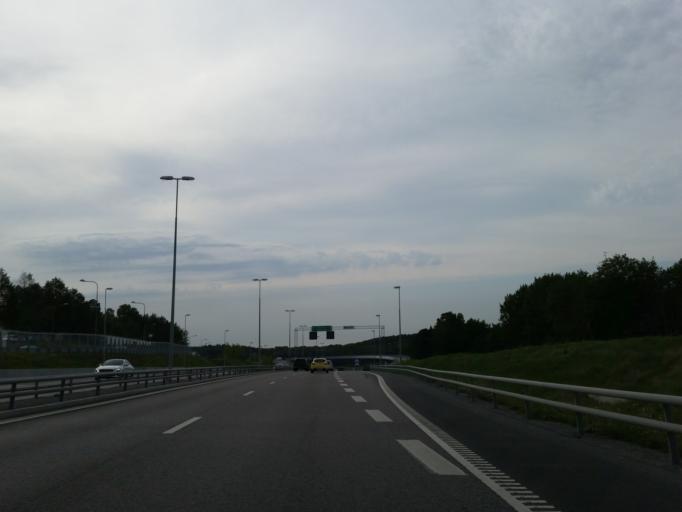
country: SE
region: Stockholm
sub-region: Stockholms Kommun
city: Kista
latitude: 59.3955
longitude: 17.9174
